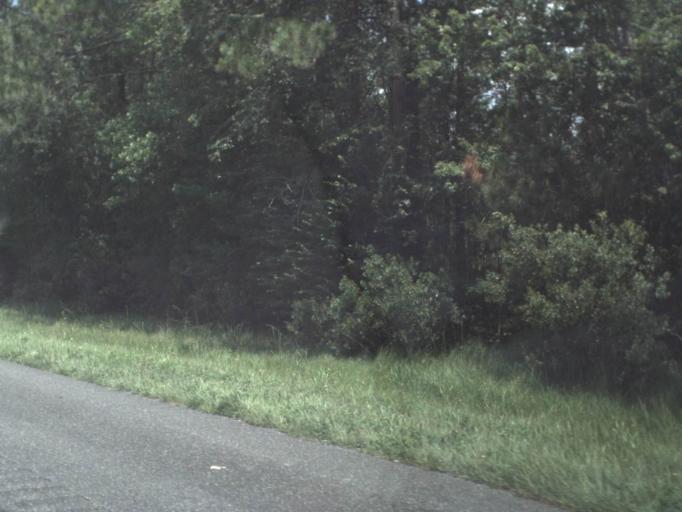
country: US
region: Florida
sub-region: Baker County
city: Macclenny
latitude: 30.2508
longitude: -82.2150
